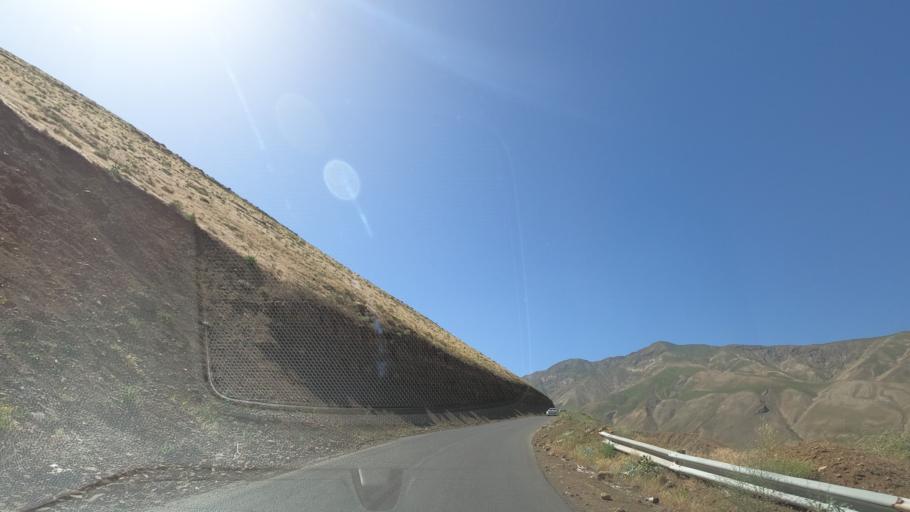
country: IR
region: Alborz
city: Karaj
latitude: 35.9349
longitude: 51.0818
